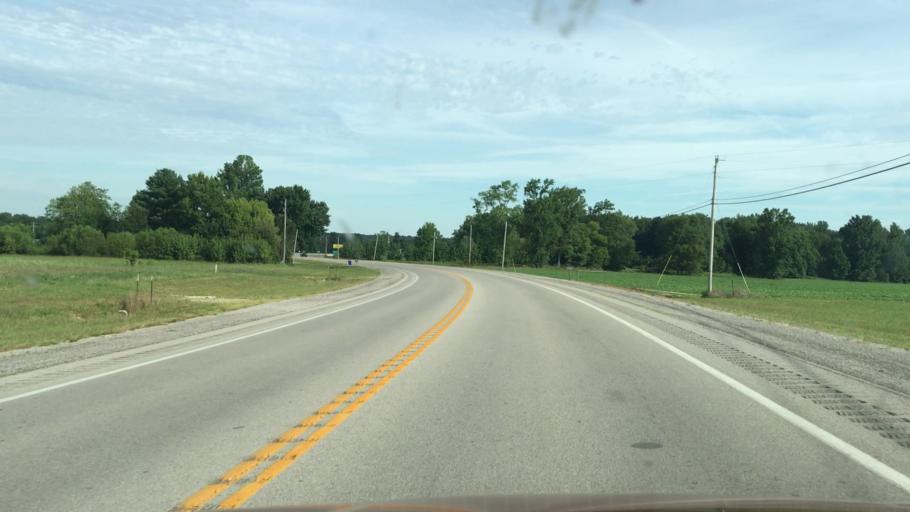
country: US
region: Kentucky
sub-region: Edmonson County
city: Brownsville
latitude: 37.1163
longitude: -86.2296
